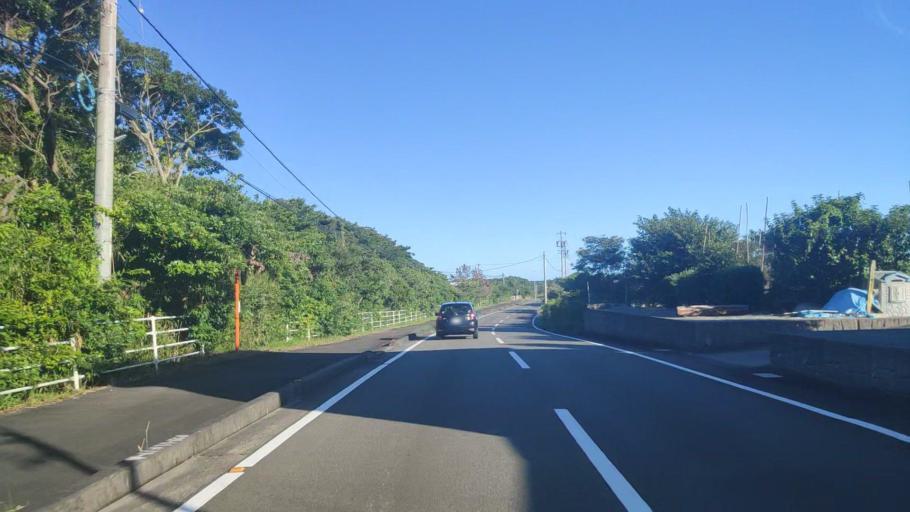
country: JP
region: Mie
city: Toba
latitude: 34.3274
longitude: 136.8743
